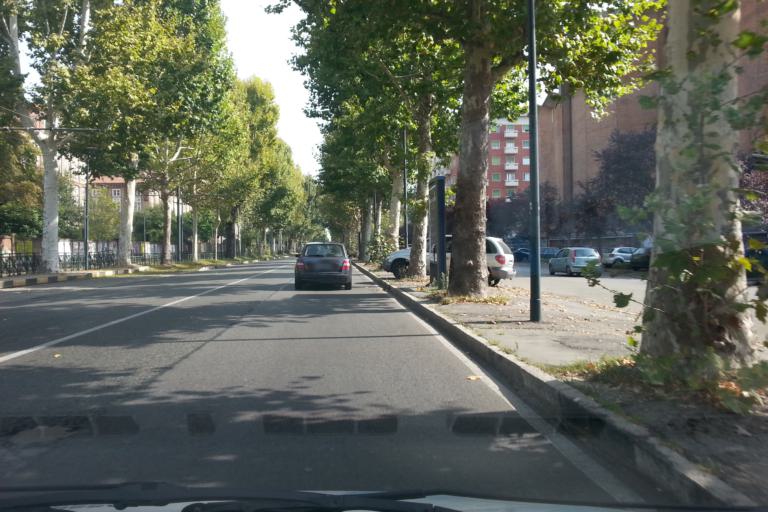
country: IT
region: Piedmont
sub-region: Provincia di Torino
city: Lesna
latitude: 45.0355
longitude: 7.6496
